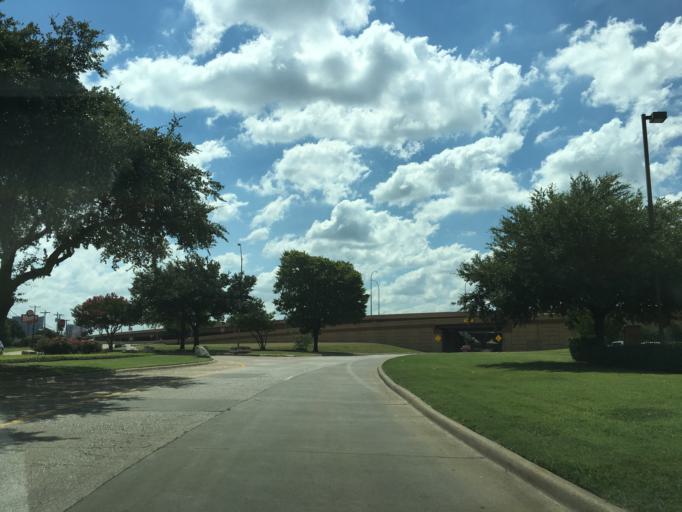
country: US
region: Texas
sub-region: Dallas County
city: Addison
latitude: 32.9252
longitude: -96.8427
